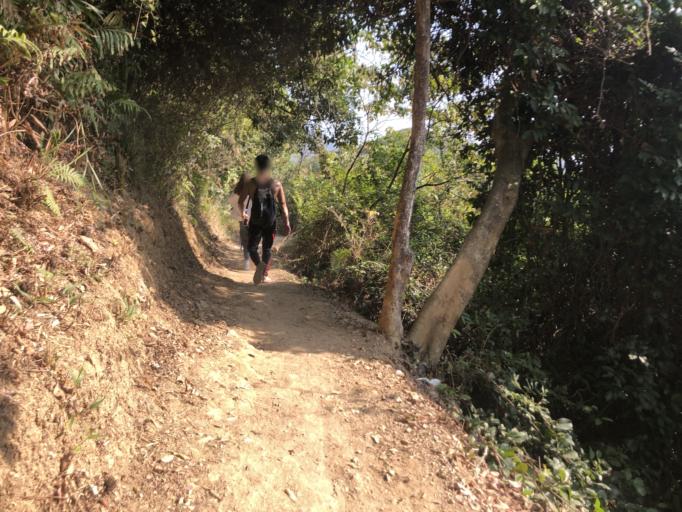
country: HK
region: Sai Kung
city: Sai Kung
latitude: 22.3652
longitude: 114.2916
